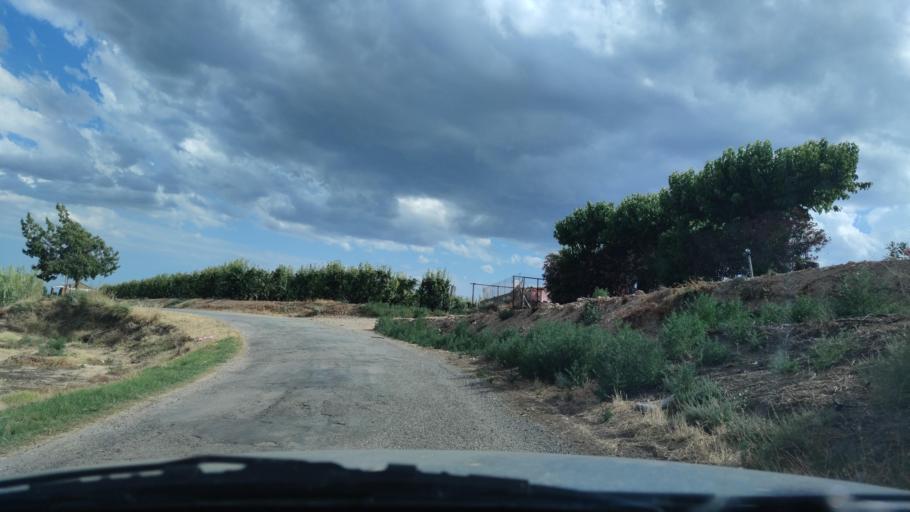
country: ES
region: Catalonia
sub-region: Provincia de Lleida
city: Alcarras
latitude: 41.6042
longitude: 0.5431
